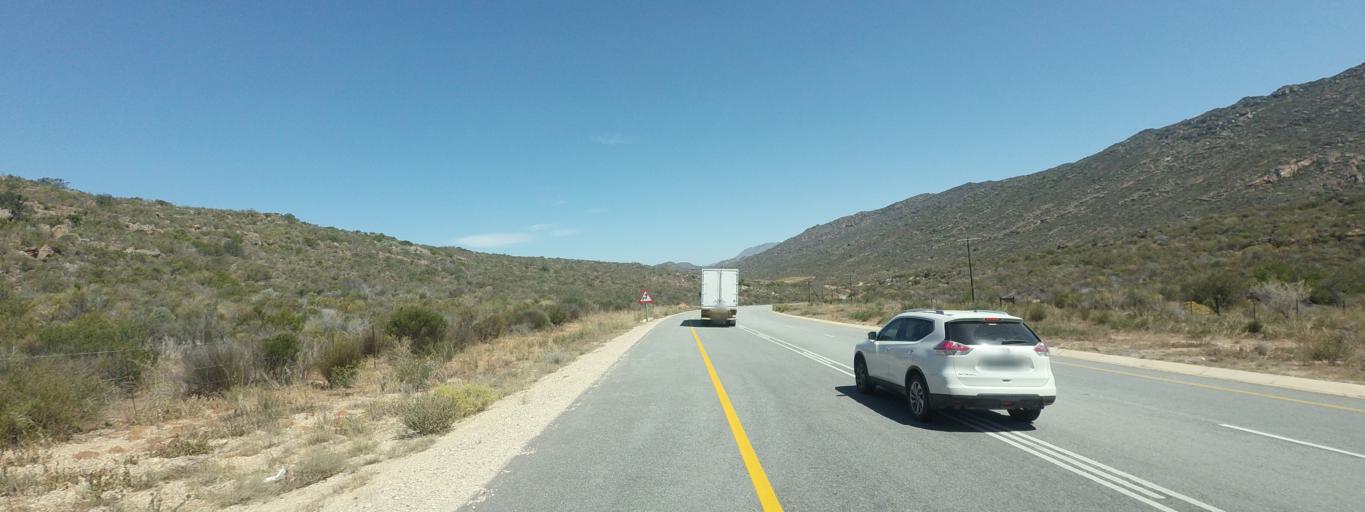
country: ZA
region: Western Cape
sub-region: West Coast District Municipality
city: Clanwilliam
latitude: -32.3327
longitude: 18.9247
